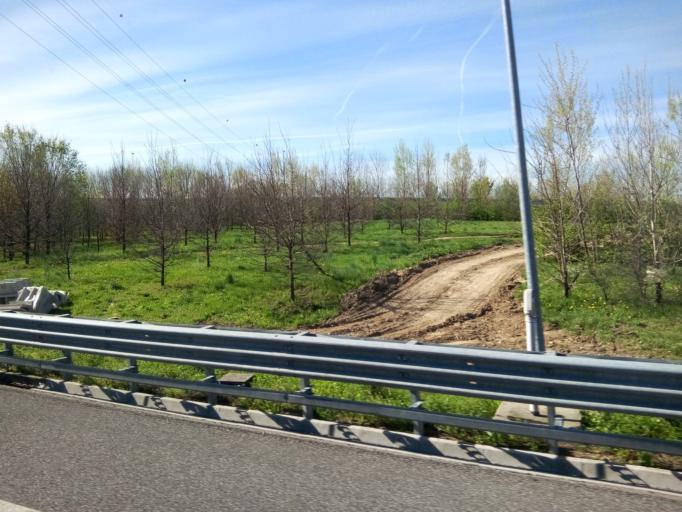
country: IT
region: Lombardy
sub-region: Citta metropolitana di Milano
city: Pero
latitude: 45.5304
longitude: 9.0928
